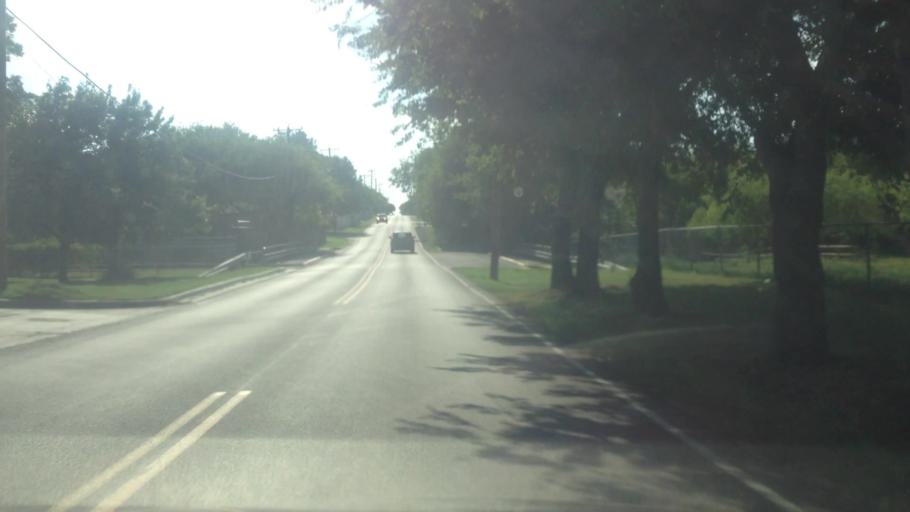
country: US
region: Texas
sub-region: Tarrant County
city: Watauga
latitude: 32.8677
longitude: -97.2441
